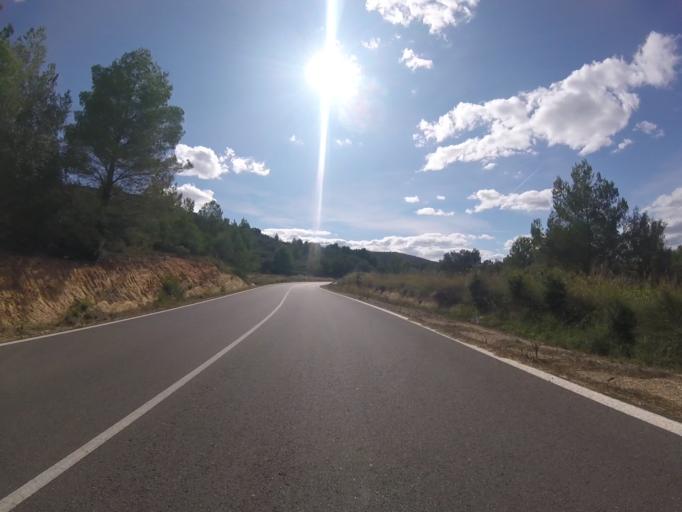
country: ES
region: Valencia
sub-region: Provincia de Castello
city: Cati
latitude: 40.4342
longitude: 0.0963
